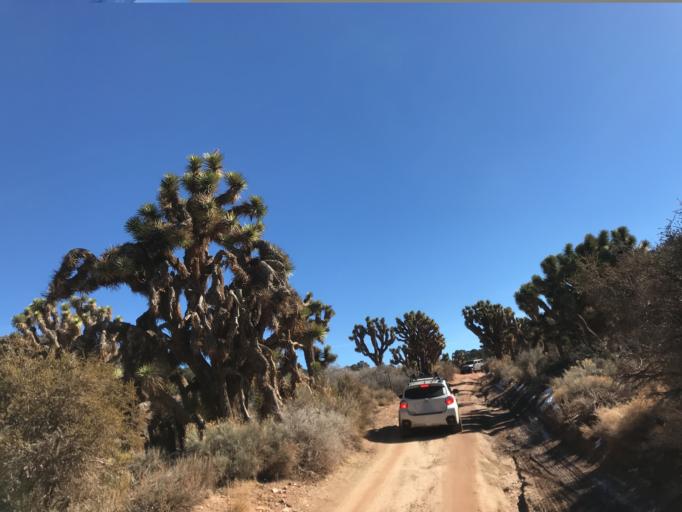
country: US
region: California
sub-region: San Bernardino County
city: Big Bear City
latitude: 34.2459
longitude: -116.7025
